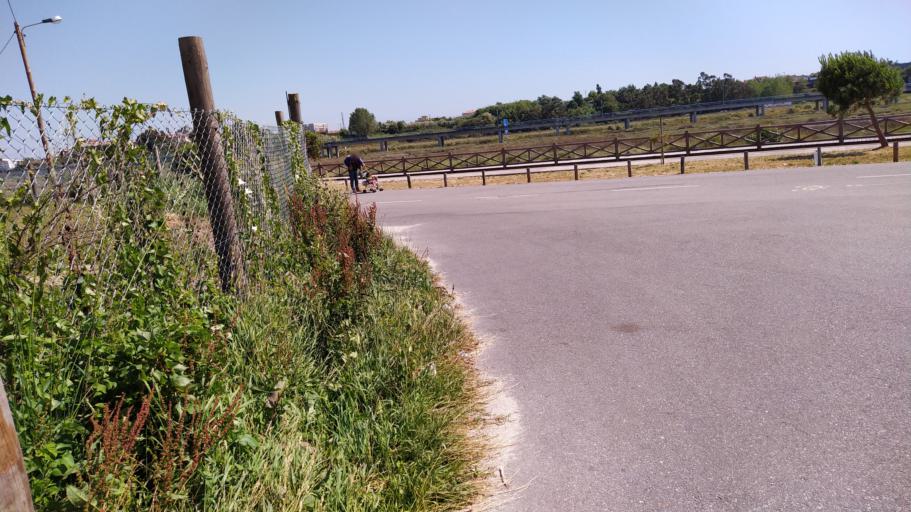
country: PT
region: Aveiro
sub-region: Aveiro
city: Aveiro
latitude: 40.6573
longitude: -8.6361
